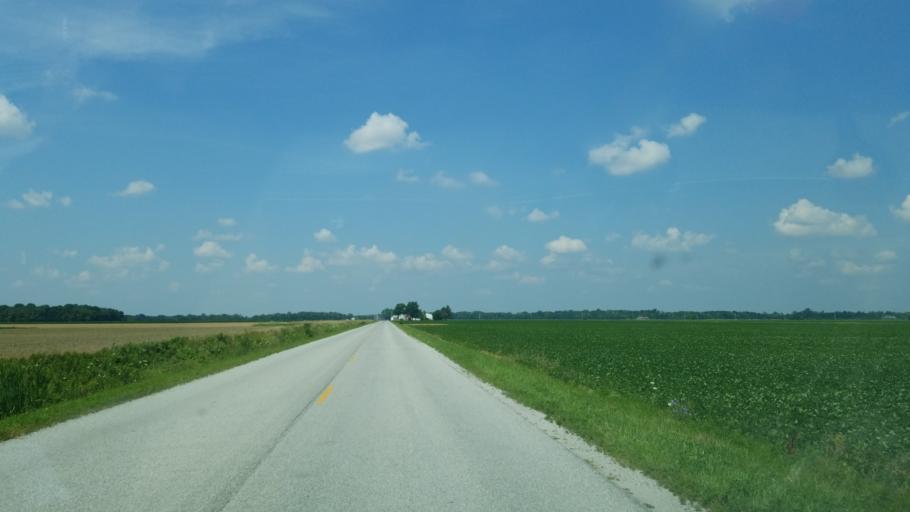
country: US
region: Ohio
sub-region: Seneca County
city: Fostoria
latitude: 41.2387
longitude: -83.5033
